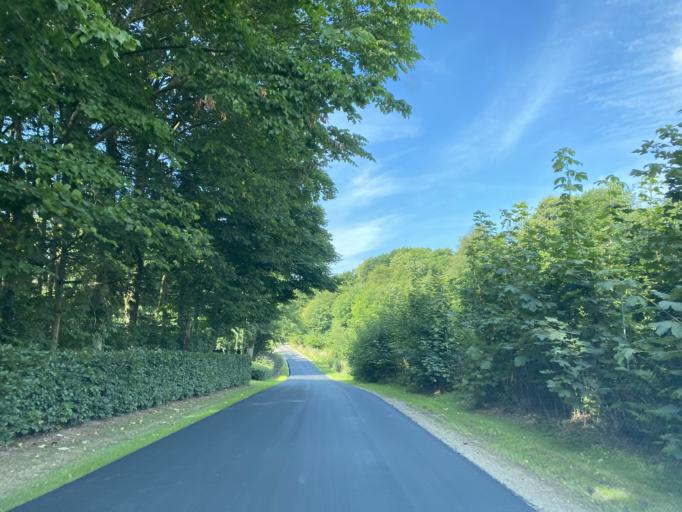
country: DK
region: Central Jutland
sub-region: Favrskov Kommune
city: Hammel
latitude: 56.2534
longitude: 9.8269
